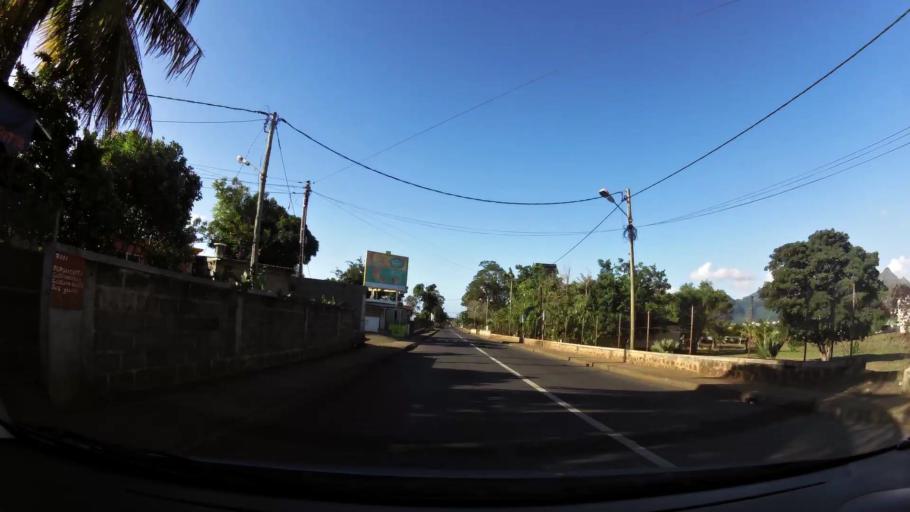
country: MU
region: Black River
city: Petite Riviere
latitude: -20.1936
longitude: 57.4497
